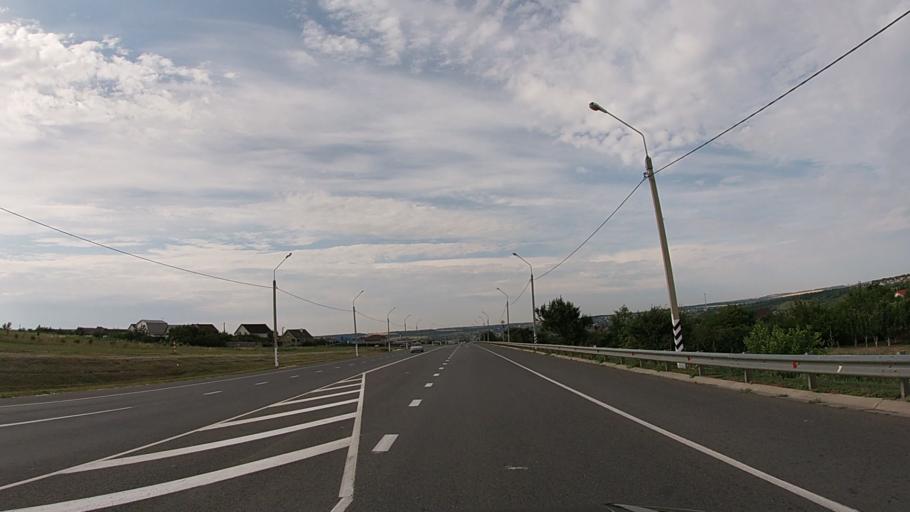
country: RU
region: Belgorod
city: Severnyy
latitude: 50.6504
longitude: 36.4676
